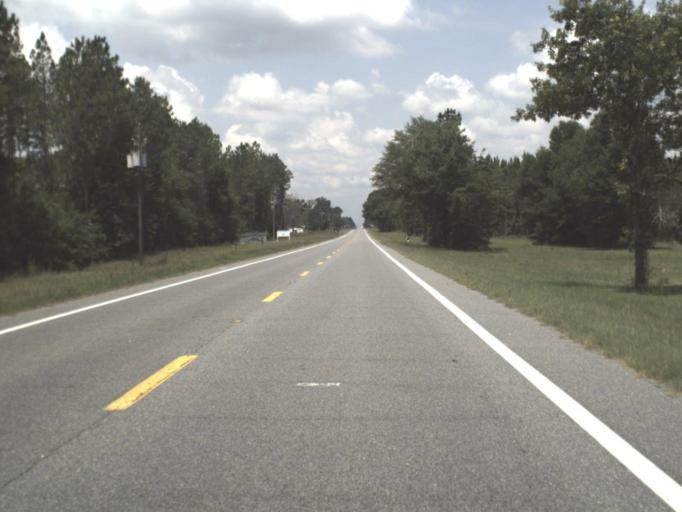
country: US
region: Florida
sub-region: Hamilton County
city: Jasper
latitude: 30.4903
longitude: -83.1045
